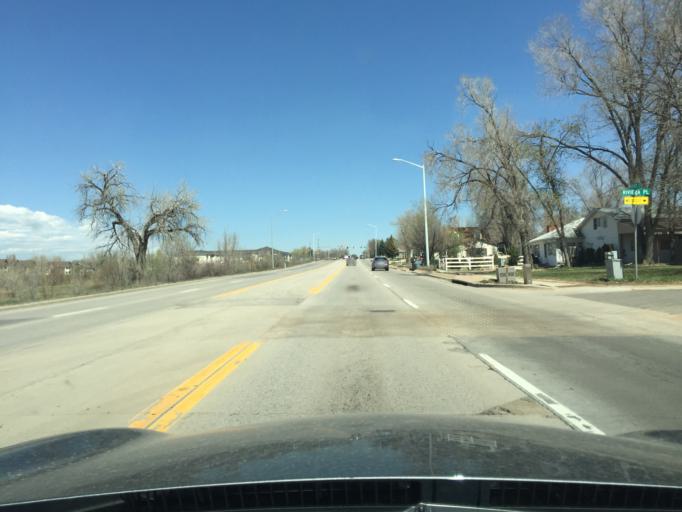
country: US
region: Colorado
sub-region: Boulder County
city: Longmont
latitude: 40.1716
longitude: -105.1308
